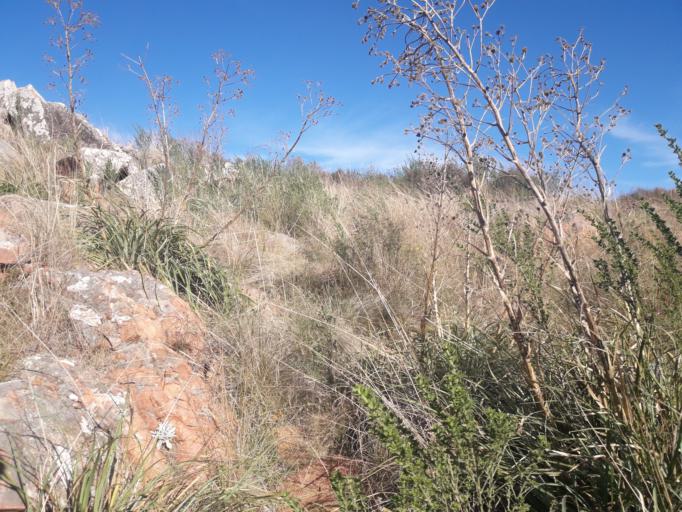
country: AR
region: Buenos Aires
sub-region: Partido de Tandil
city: Tandil
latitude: -37.3440
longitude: -59.1216
